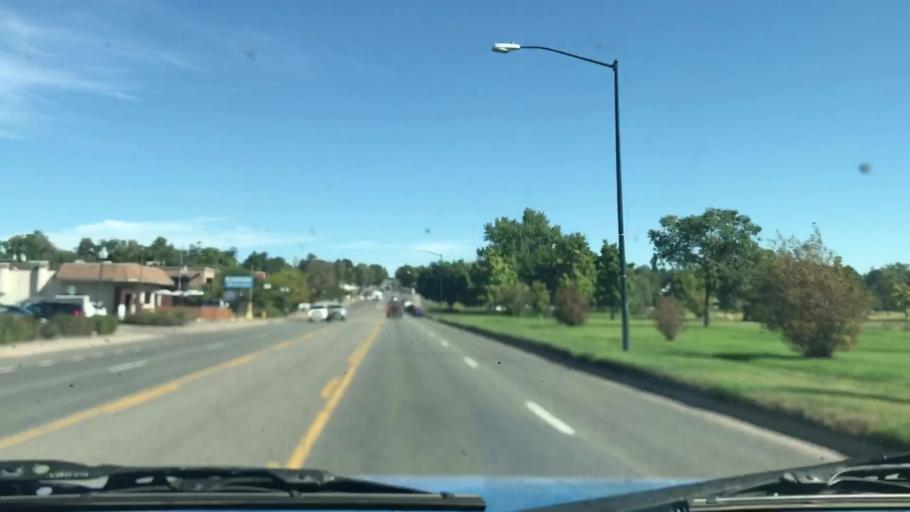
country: US
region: Colorado
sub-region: Jefferson County
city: Edgewater
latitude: 39.7494
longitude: -105.0532
